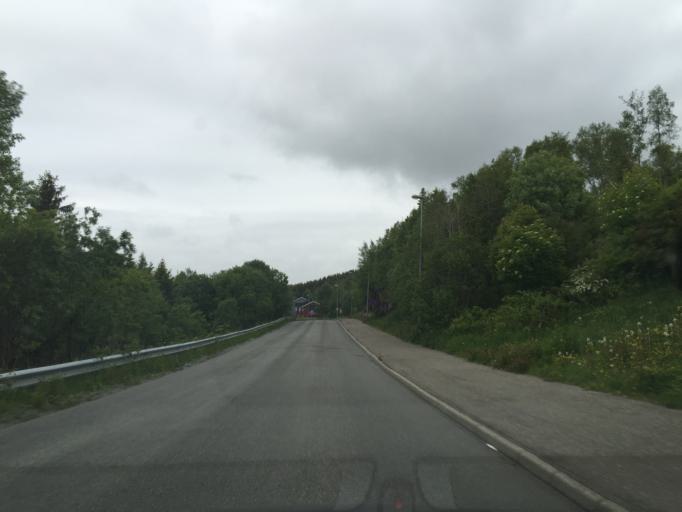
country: NO
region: Nordland
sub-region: Bodo
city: Lopsmarka
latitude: 67.2933
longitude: 14.5907
